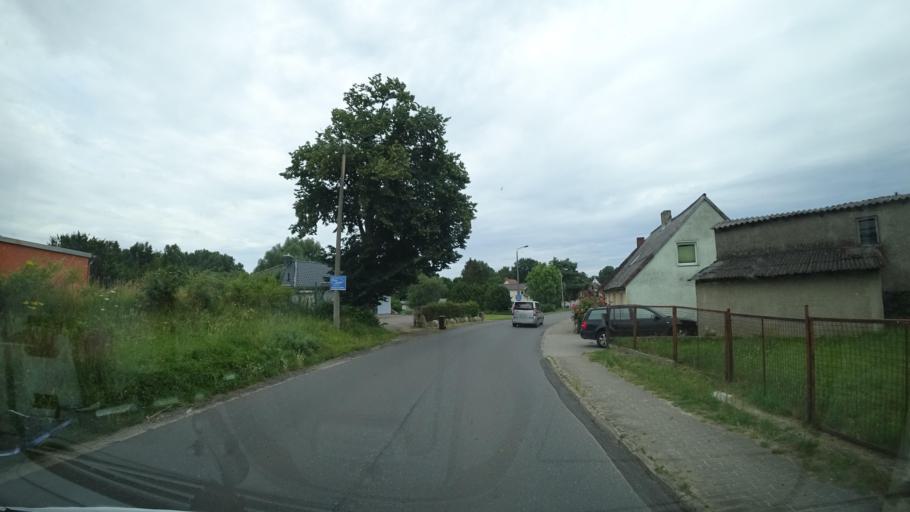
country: DE
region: Mecklenburg-Vorpommern
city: Sehlen
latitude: 54.3402
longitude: 13.4189
